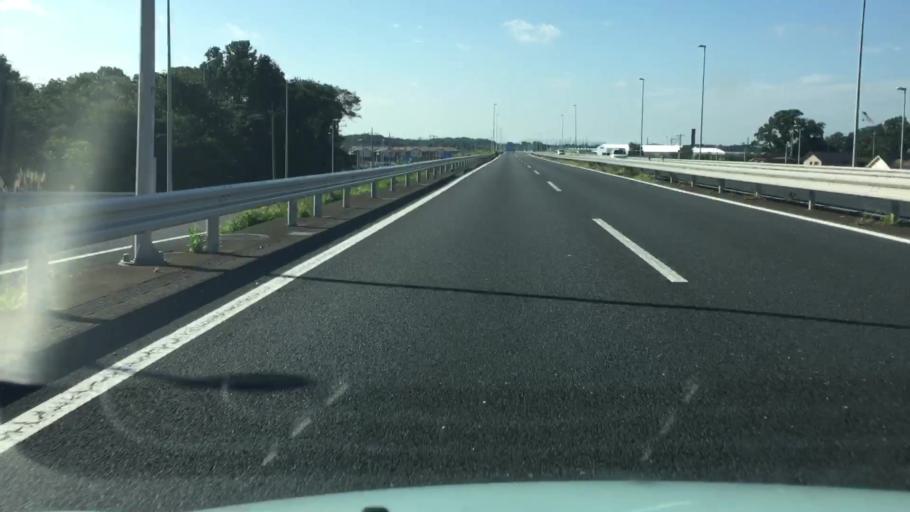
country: JP
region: Tochigi
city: Mooka
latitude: 36.4587
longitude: 139.9796
